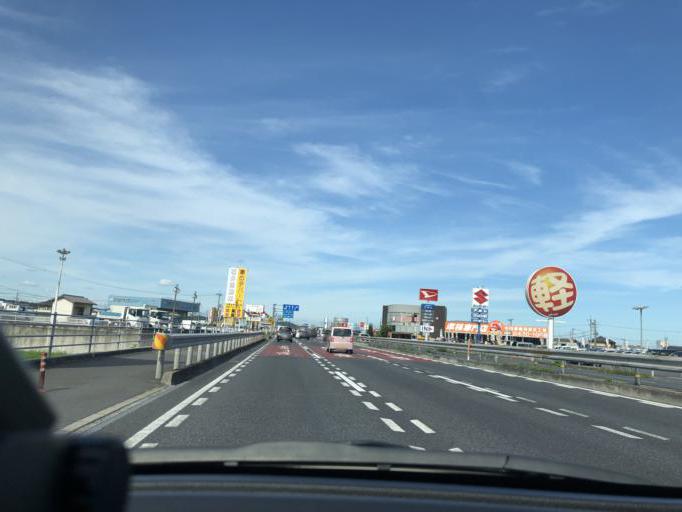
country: JP
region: Okayama
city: Kurashiki
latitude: 34.5886
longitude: 133.7941
